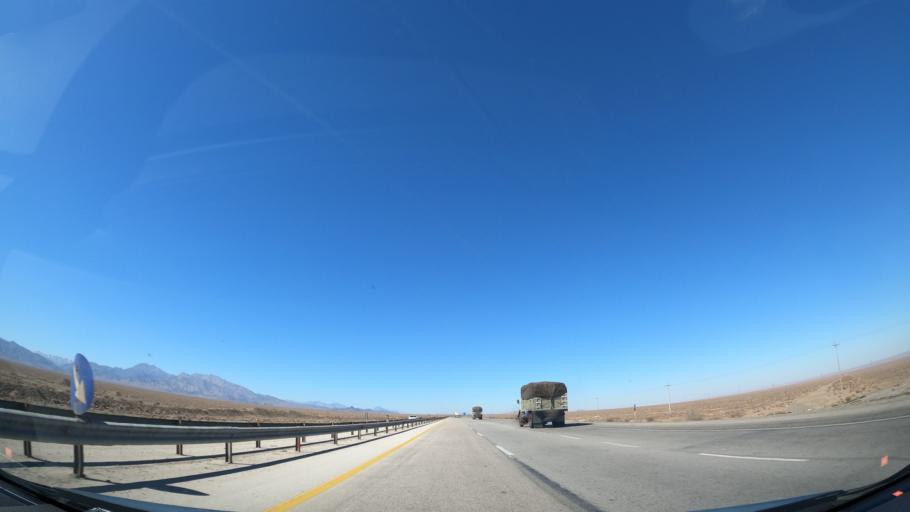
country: IR
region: Isfahan
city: Natanz
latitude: 33.6587
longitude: 51.8714
